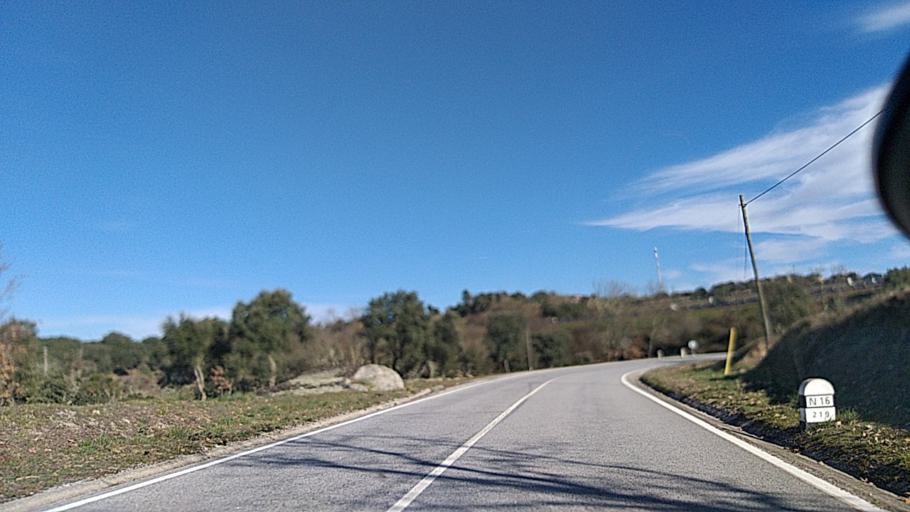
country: ES
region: Castille and Leon
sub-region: Provincia de Salamanca
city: Fuentes de Onoro
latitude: 40.6138
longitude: -6.8901
